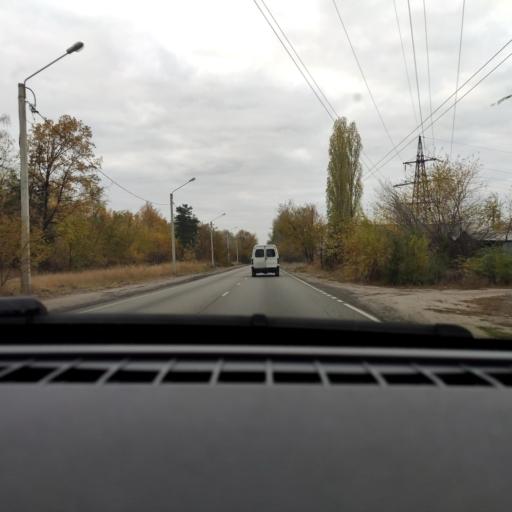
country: RU
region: Voronezj
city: Somovo
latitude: 51.7265
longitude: 39.2964
